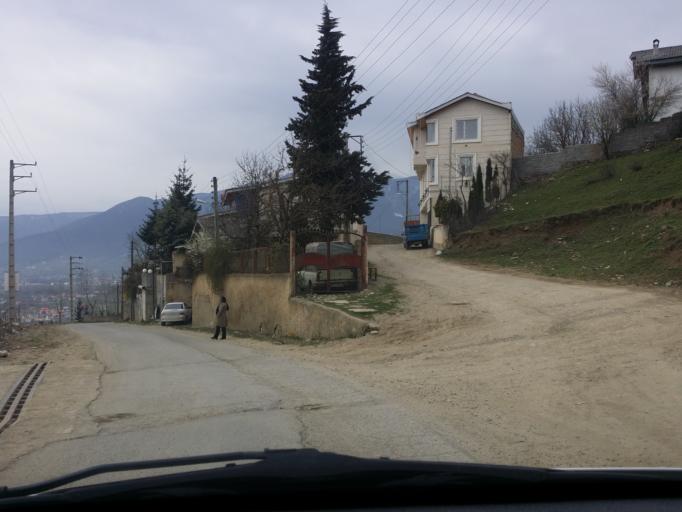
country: IR
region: Mazandaran
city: `Abbasabad
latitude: 36.5348
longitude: 51.1607
